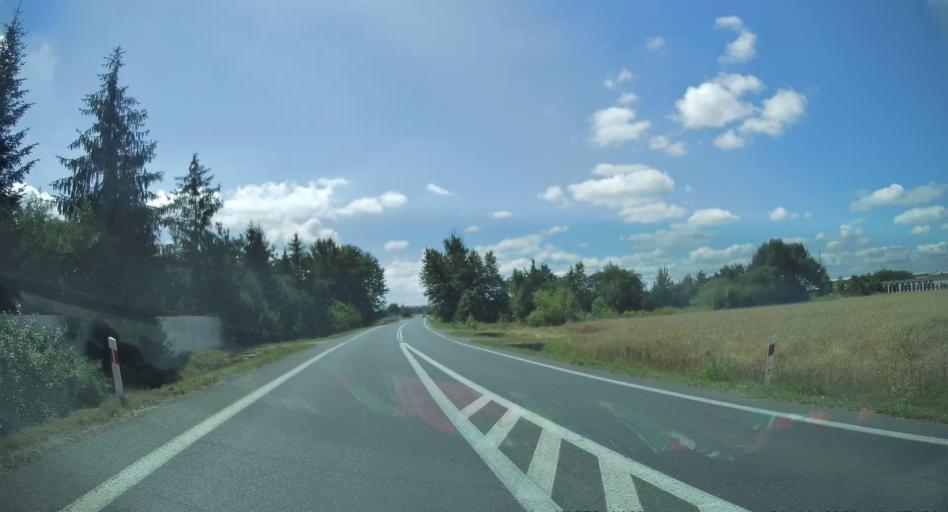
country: PL
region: Subcarpathian Voivodeship
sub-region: Powiat debicki
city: Brzeznica
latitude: 50.1460
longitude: 21.4862
